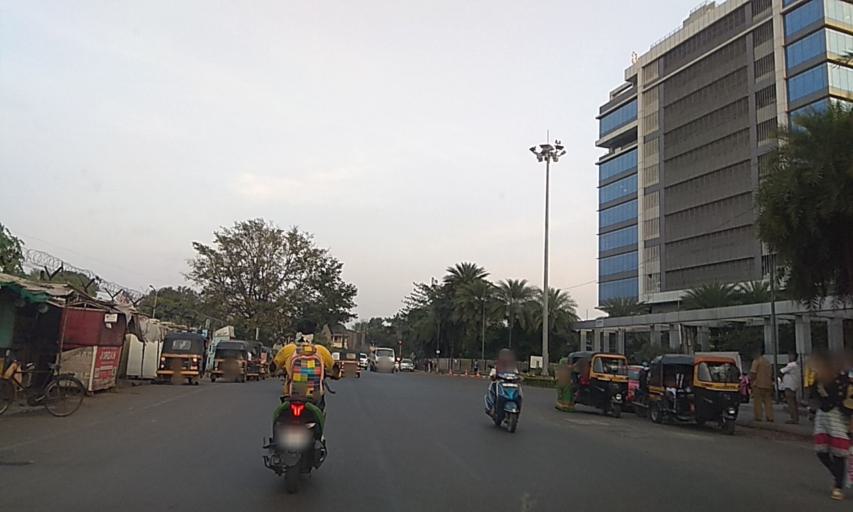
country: IN
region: Maharashtra
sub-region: Pune Division
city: Khadki
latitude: 18.5643
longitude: 73.8839
